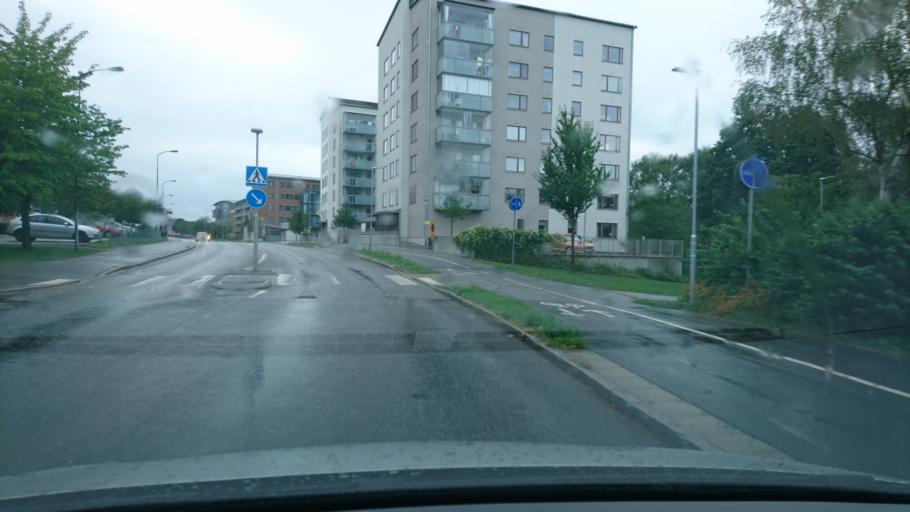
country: SE
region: Uppsala
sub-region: Uppsala Kommun
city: Uppsala
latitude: 59.8695
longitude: 17.6191
